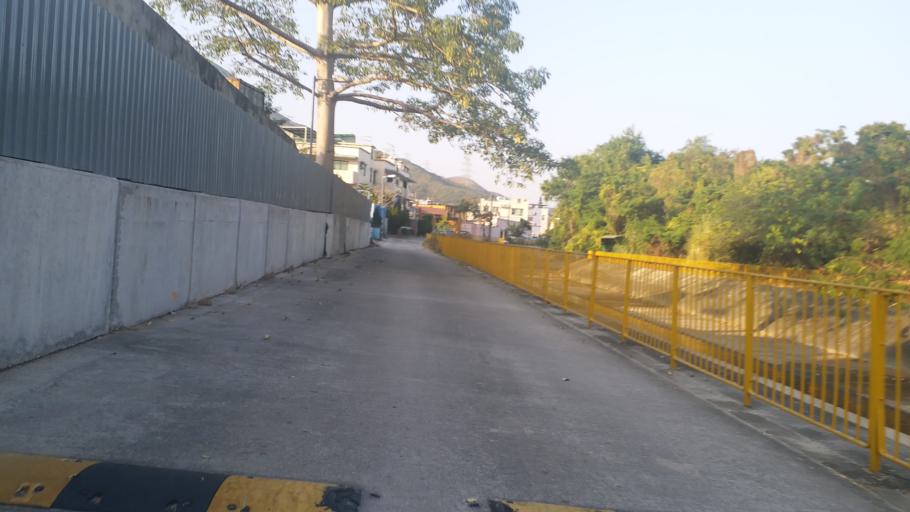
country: HK
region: Tuen Mun
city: Tuen Mun
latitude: 22.4181
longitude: 113.9810
